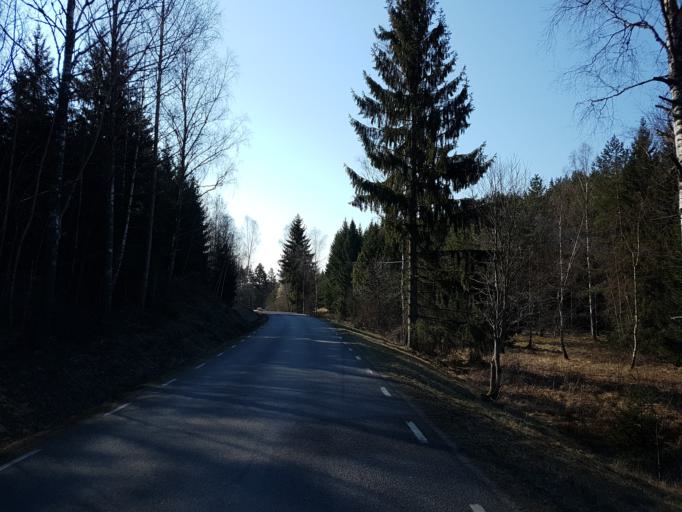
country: SE
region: Kalmar
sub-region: Vasterviks Kommun
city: Overum
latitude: 58.1832
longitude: 16.2800
